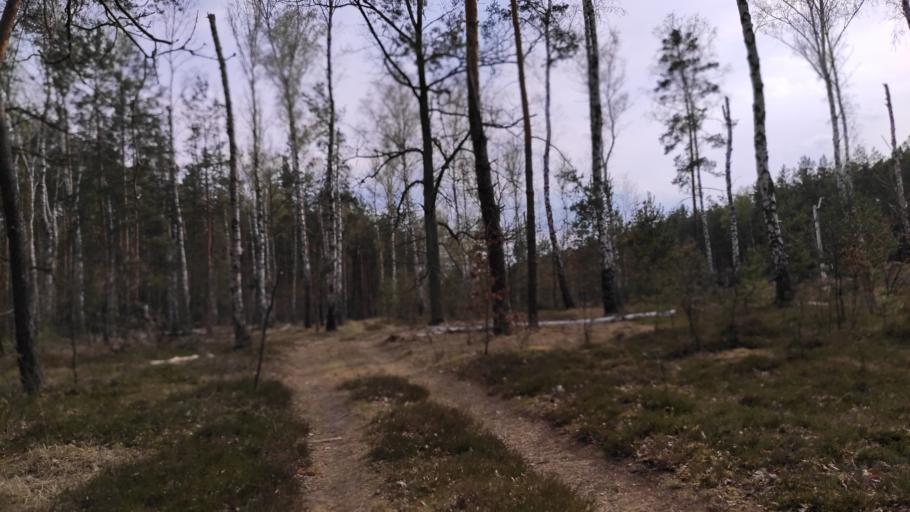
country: PL
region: Masovian Voivodeship
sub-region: Powiat grojecki
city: Warka
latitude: 51.7613
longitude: 21.1873
